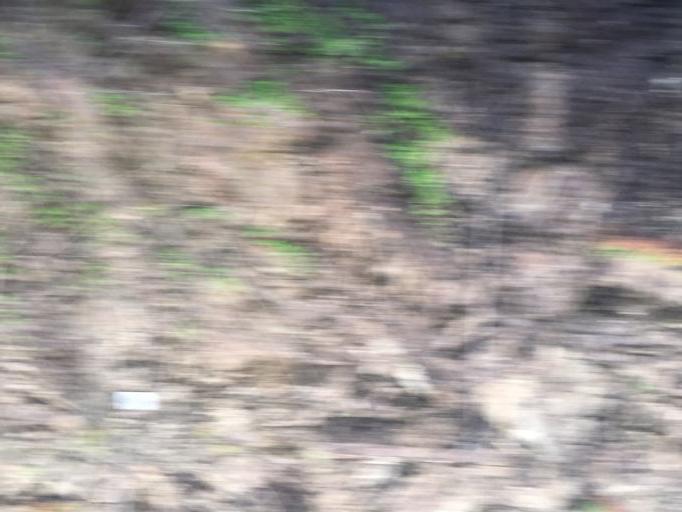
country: FR
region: Rhone-Alpes
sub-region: Departement de l'Ardeche
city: Tournon-sur-Rhone
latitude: 45.0762
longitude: 4.8306
